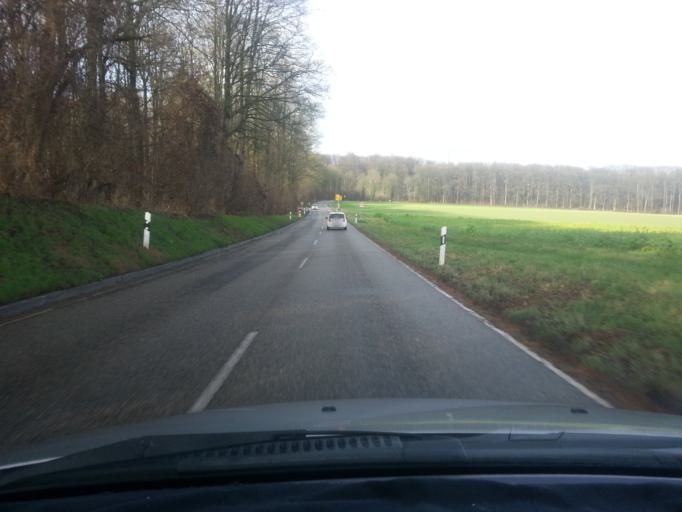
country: DE
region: Baden-Wuerttemberg
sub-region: Karlsruhe Region
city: Zaisenhausen
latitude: 49.1836
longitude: 8.8341
